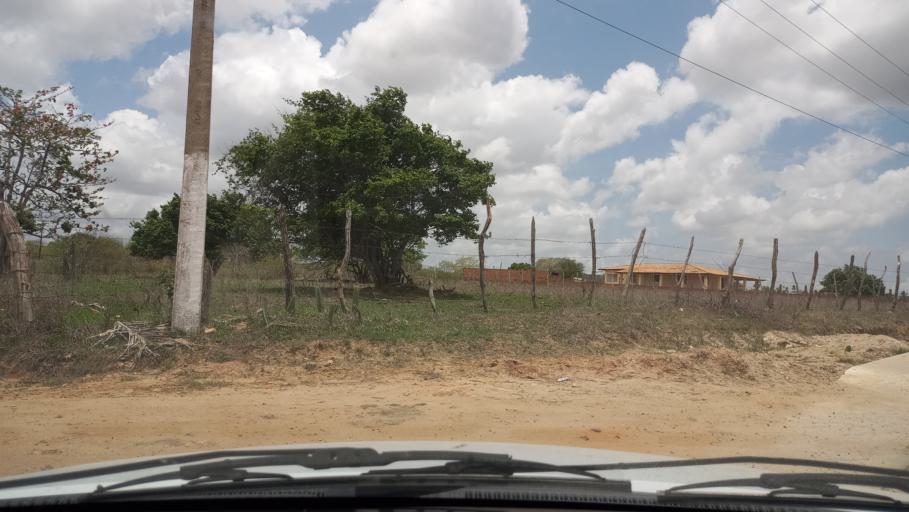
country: BR
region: Rio Grande do Norte
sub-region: Brejinho
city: Brejinho
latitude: -6.2747
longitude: -35.3319
